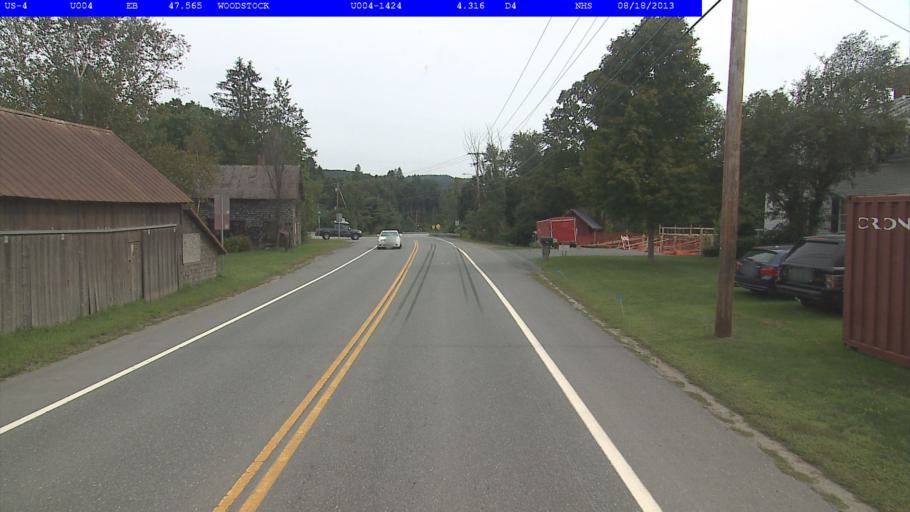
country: US
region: Vermont
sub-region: Windsor County
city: Woodstock
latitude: 43.6107
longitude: -72.5496
